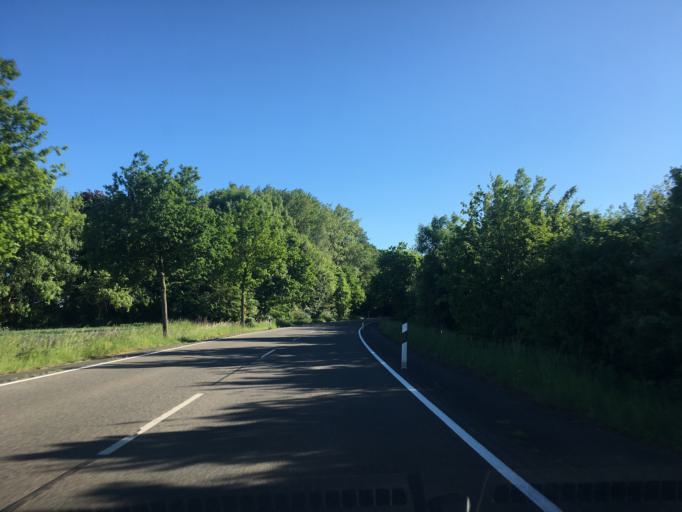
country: DE
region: North Rhine-Westphalia
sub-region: Regierungsbezirk Munster
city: Senden
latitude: 51.9020
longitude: 7.5285
